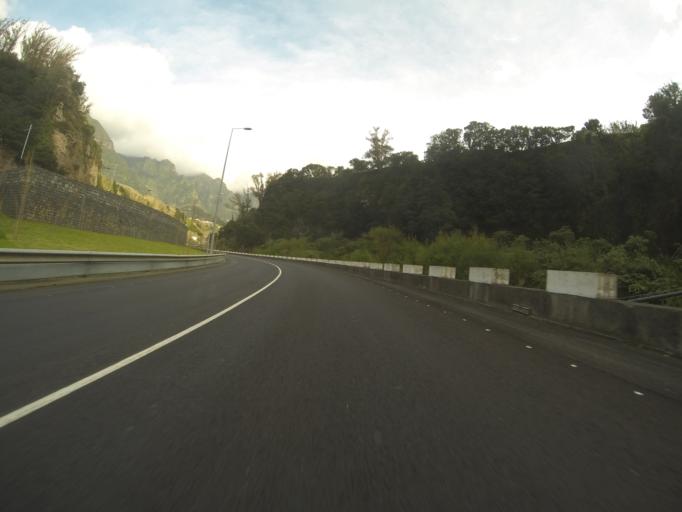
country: PT
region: Madeira
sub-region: Sao Vicente
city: Sao Vicente
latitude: 32.7947
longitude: -17.0397
